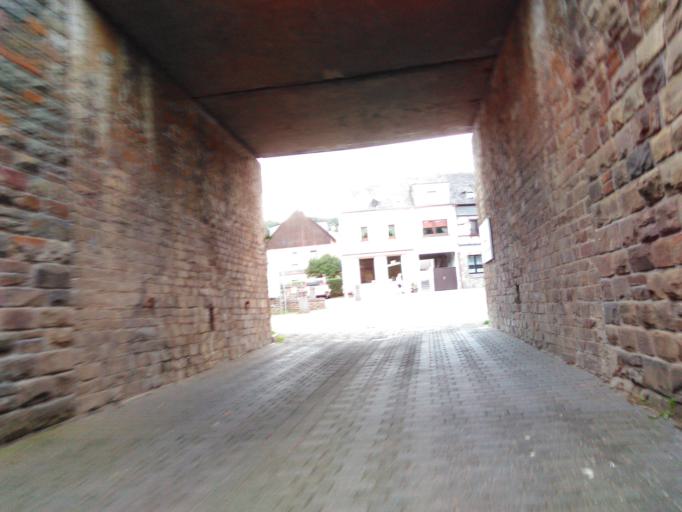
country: DE
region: Rheinland-Pfalz
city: Dieblich
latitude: 50.3096
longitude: 7.4607
